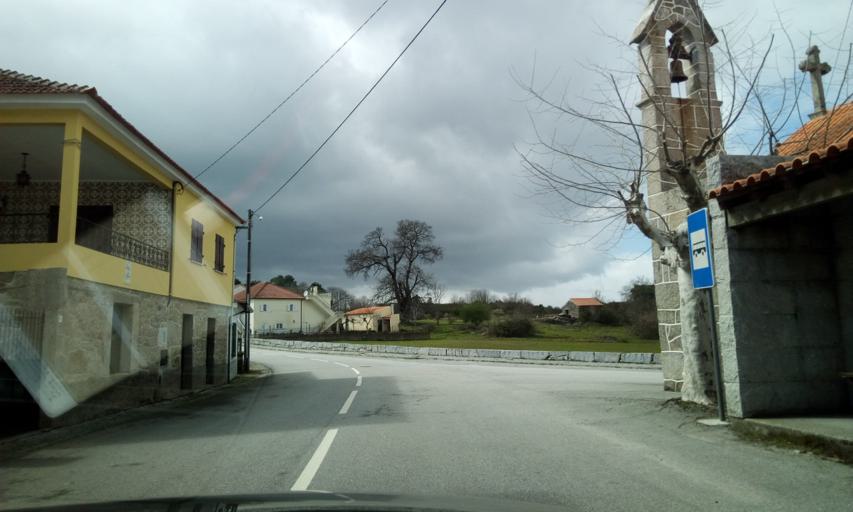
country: PT
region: Guarda
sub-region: Fornos de Algodres
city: Fornos de Algodres
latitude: 40.6364
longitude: -7.5598
